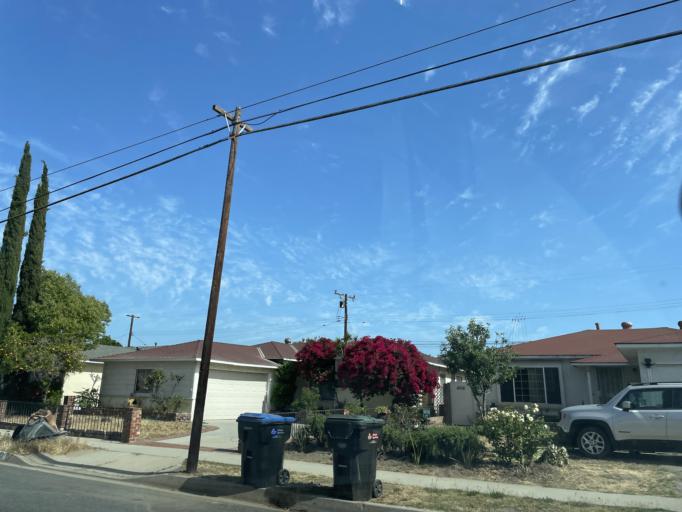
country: US
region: California
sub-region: Los Angeles County
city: Norwalk
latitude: 33.9097
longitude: -118.0596
